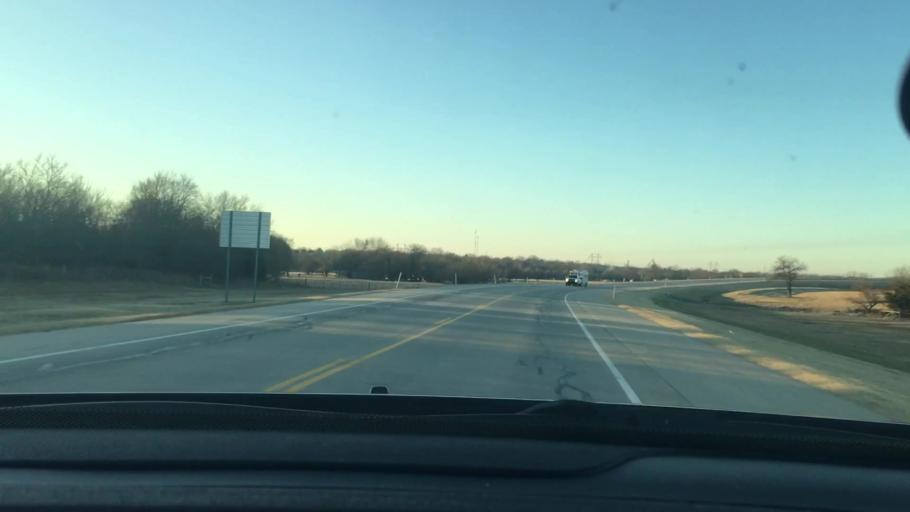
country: US
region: Oklahoma
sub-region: Murray County
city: Sulphur
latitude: 34.6418
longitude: -96.8405
